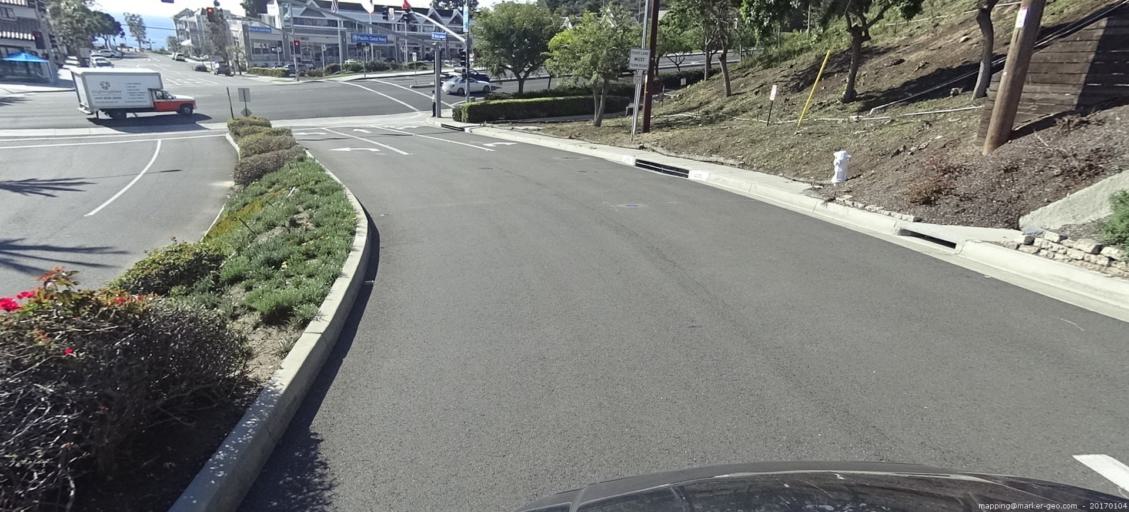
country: US
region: California
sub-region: Orange County
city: Dana Point
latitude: 33.4662
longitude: -117.7065
